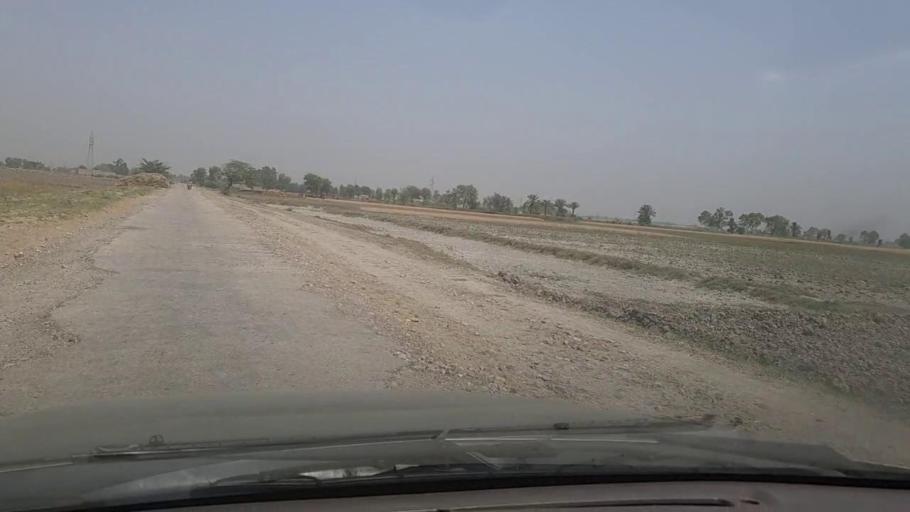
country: PK
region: Sindh
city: Madeji
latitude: 27.8206
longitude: 68.3964
